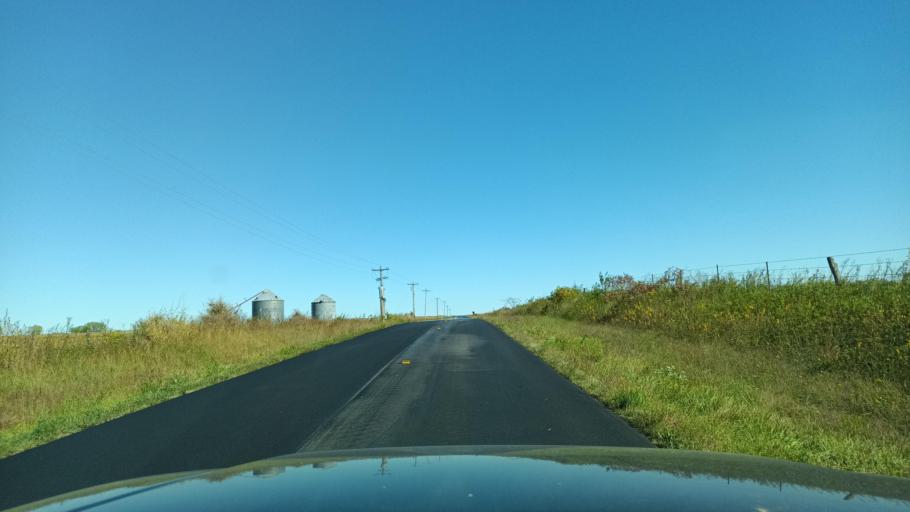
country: US
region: Missouri
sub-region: Macon County
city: La Plata
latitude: 39.9278
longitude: -92.5620
